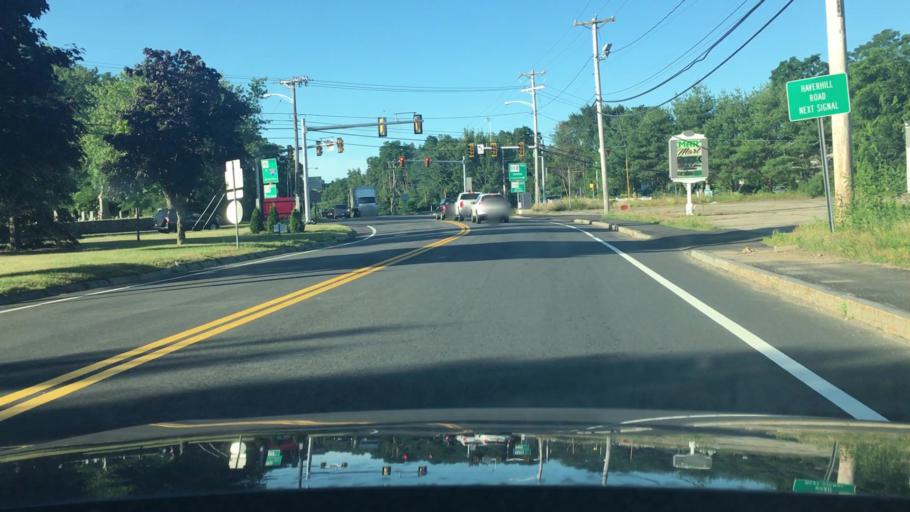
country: US
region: Massachusetts
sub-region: Essex County
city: Amesbury
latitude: 42.8454
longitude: -70.9371
